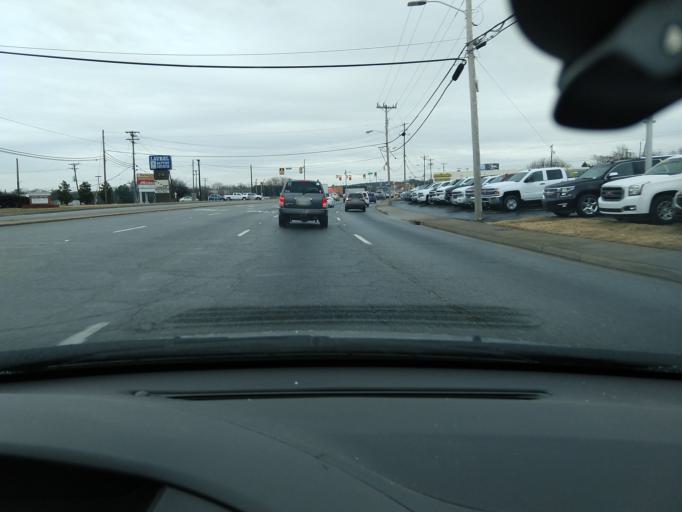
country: US
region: South Carolina
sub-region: Greenville County
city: Greenville
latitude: 34.8336
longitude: -82.3504
